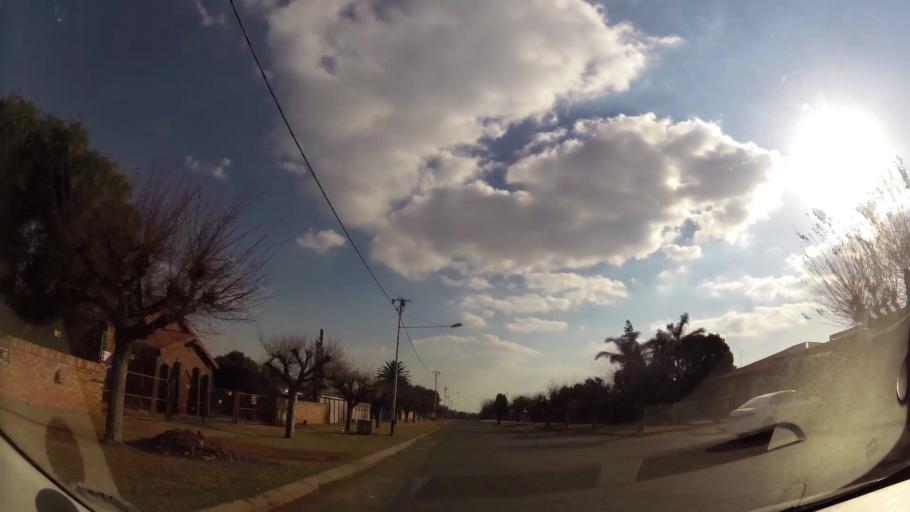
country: ZA
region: Gauteng
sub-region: West Rand District Municipality
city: Krugersdorp
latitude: -26.0873
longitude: 27.7626
